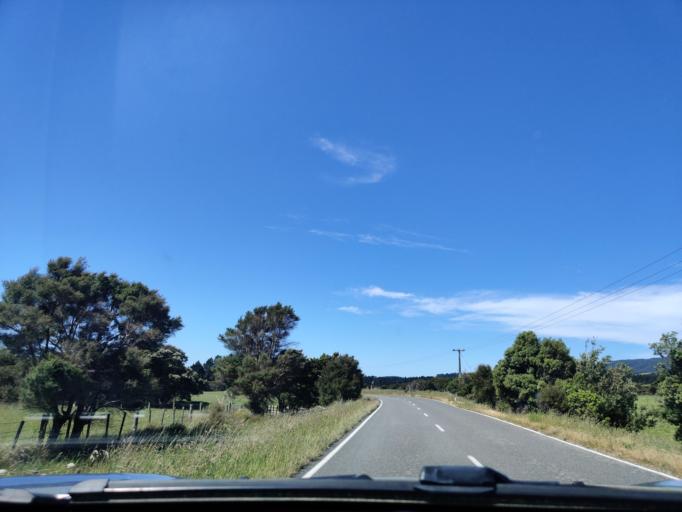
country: NZ
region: Wellington
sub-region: Upper Hutt City
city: Upper Hutt
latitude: -41.3268
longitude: 175.2422
